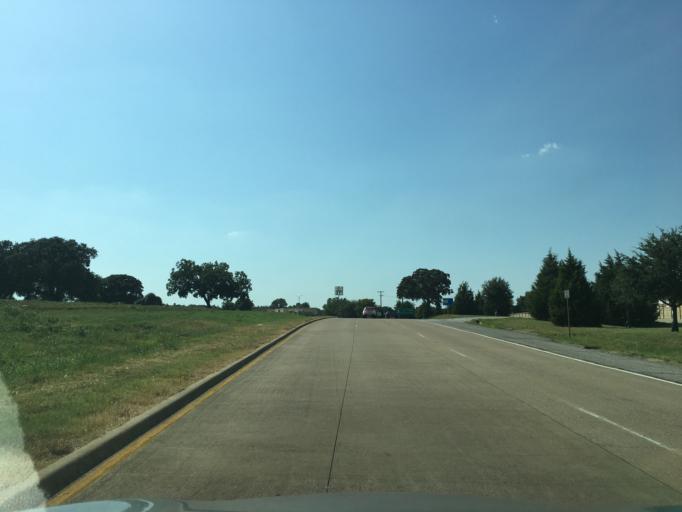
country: US
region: Texas
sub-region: Tarrant County
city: Dalworthington Gardens
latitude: 32.6758
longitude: -97.1640
